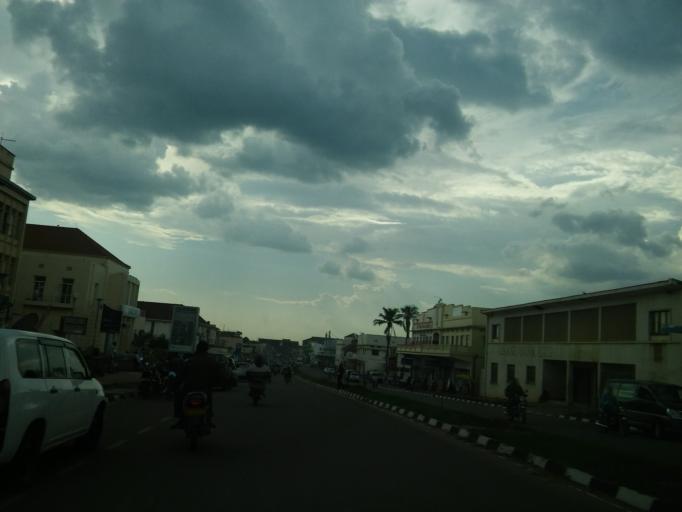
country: UG
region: Eastern Region
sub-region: Mbale District
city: Mbale
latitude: 1.0714
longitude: 34.1820
